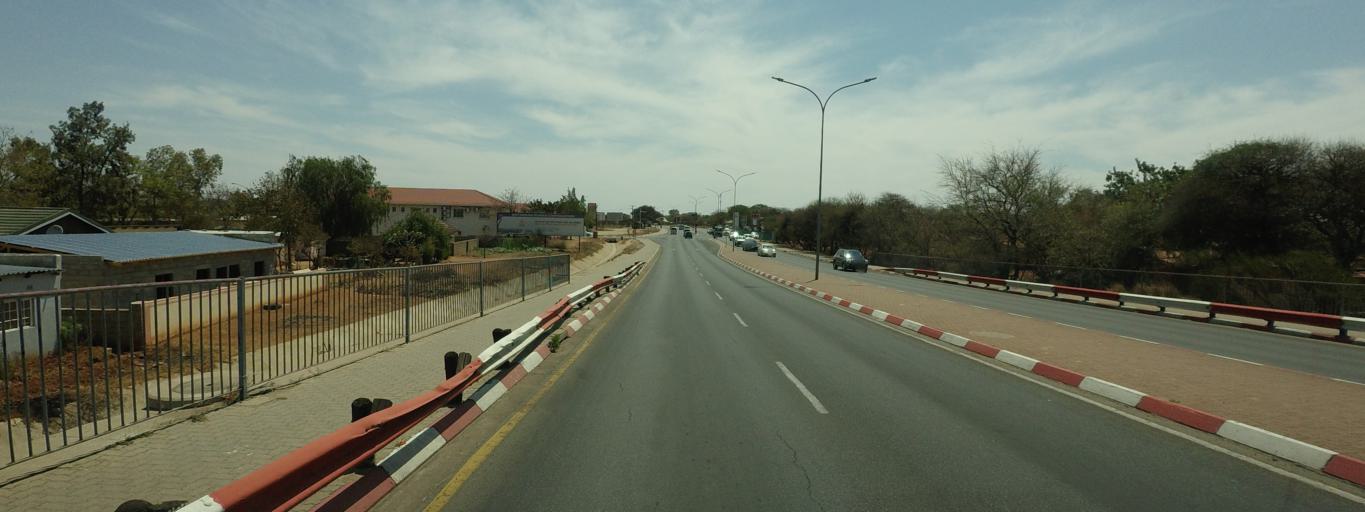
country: BW
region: North East
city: Francistown
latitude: -21.1727
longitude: 27.5084
